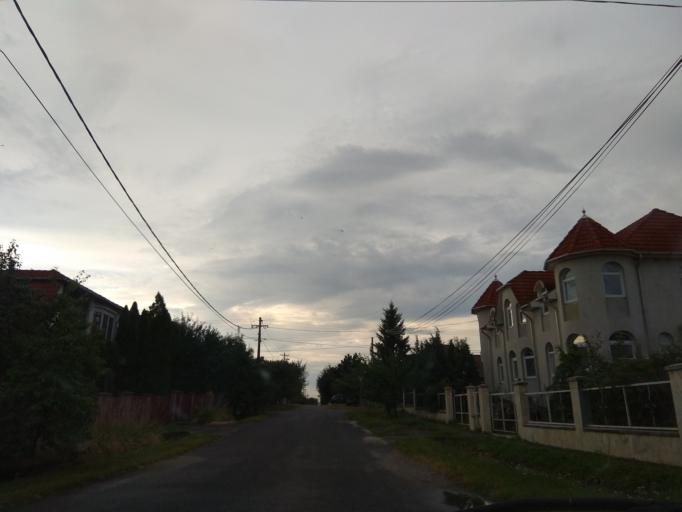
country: HU
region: Borsod-Abauj-Zemplen
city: Miskolc
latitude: 48.0736
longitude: 20.8243
